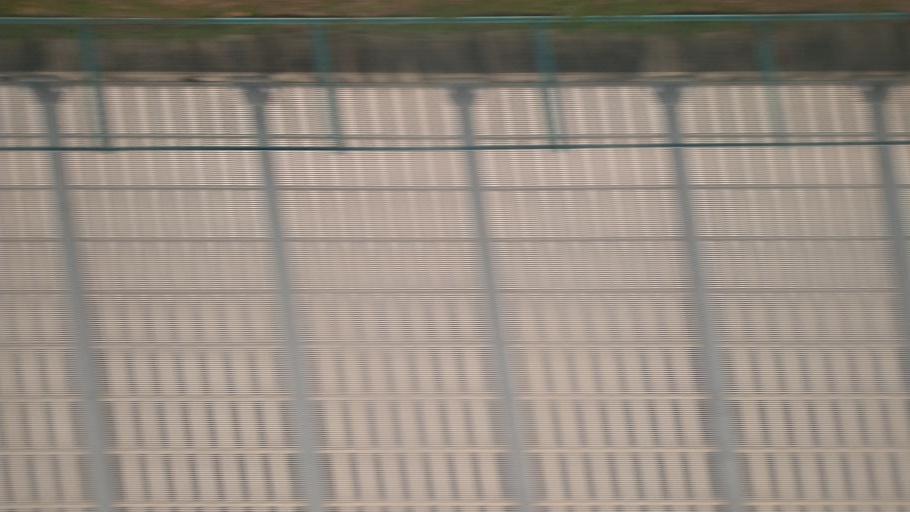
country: JP
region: Nagano
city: Matsumoto
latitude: 36.1984
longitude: 137.9652
